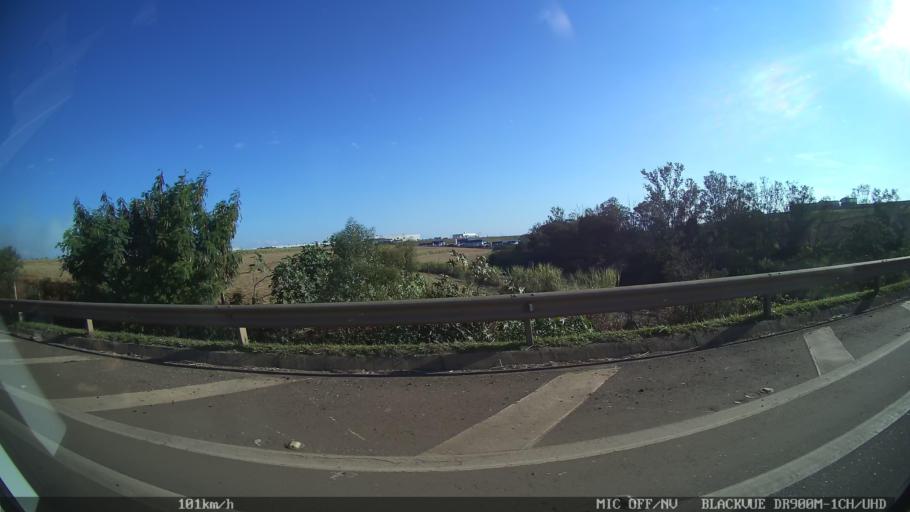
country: BR
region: Sao Paulo
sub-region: Piracicaba
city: Piracicaba
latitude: -22.6760
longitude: -47.5986
